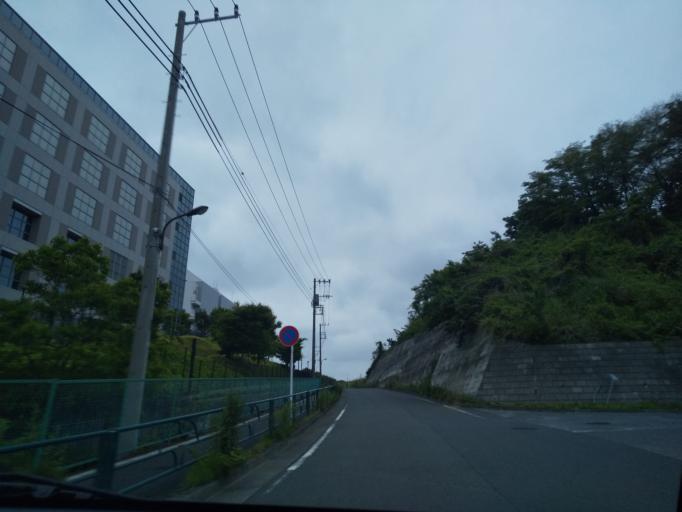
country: JP
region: Tokyo
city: Hino
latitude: 35.6109
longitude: 139.4003
